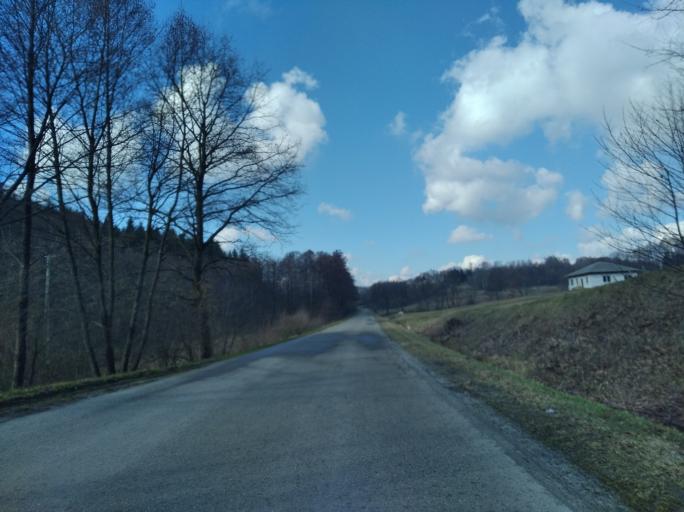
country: PL
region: Subcarpathian Voivodeship
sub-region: Powiat strzyzowski
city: Frysztak
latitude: 49.8675
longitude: 21.5389
